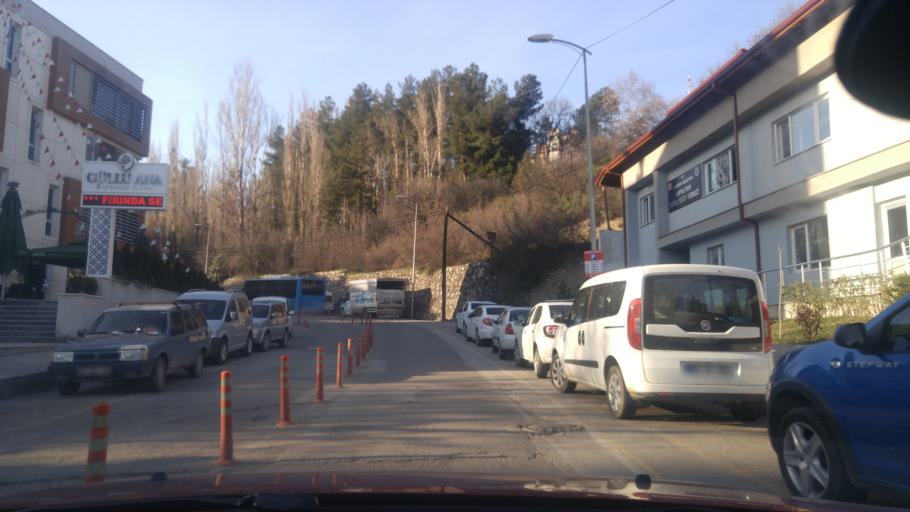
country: TR
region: Karabuk
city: Karabuk
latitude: 41.1979
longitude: 32.6178
